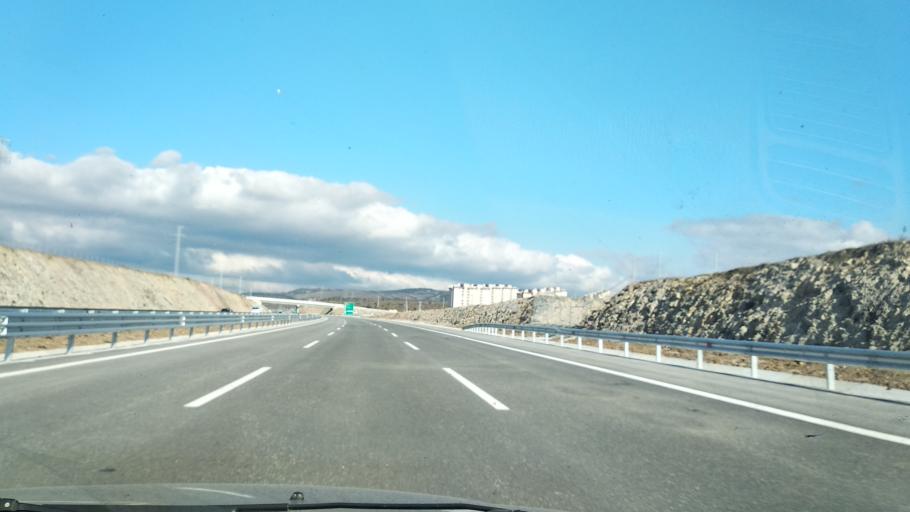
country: TR
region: Izmir
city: Yenisakran
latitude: 38.8737
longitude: 27.0863
